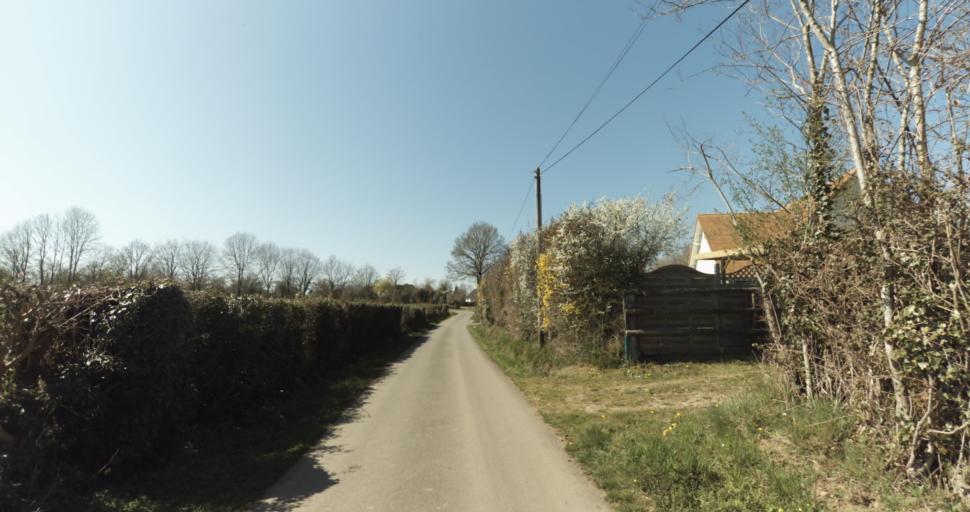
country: FR
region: Lower Normandy
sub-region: Departement du Calvados
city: Saint-Pierre-sur-Dives
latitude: 49.0036
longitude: -0.0033
